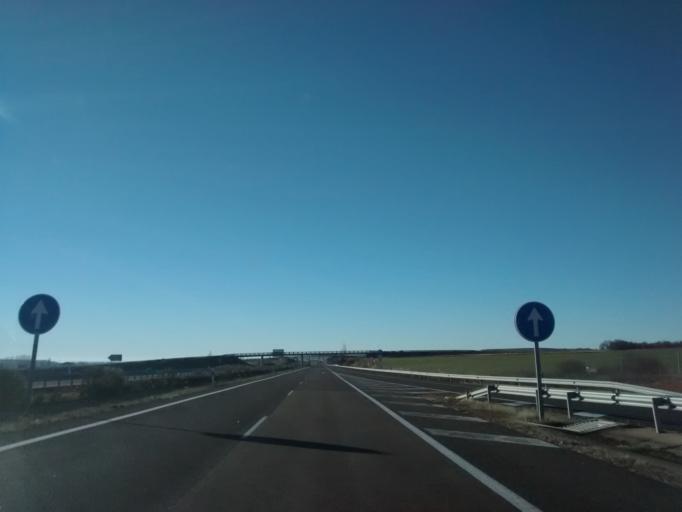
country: ES
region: Castille and Leon
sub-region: Provincia de Palencia
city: Santa Cruz de Boedo
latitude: 42.5378
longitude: -4.3803
